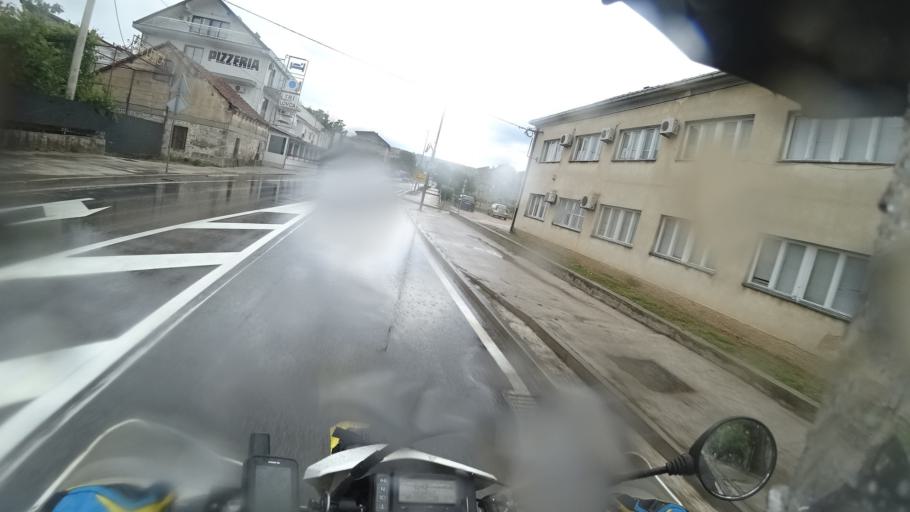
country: HR
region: Sibensko-Kniniska
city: Knin
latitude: 44.0406
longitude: 16.2011
